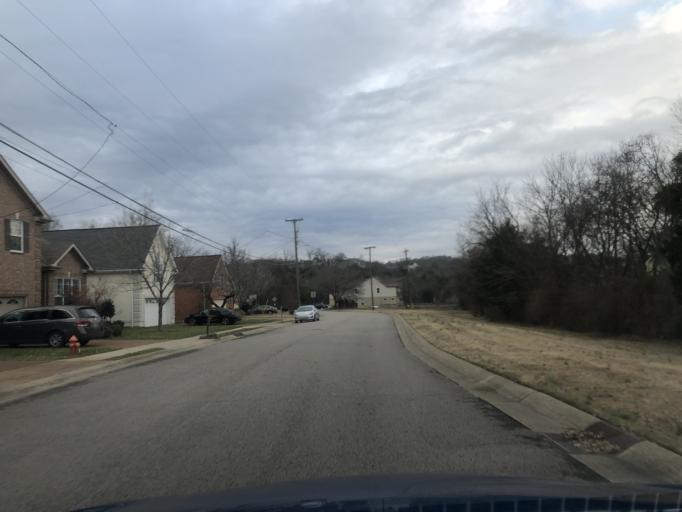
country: US
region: Tennessee
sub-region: Davidson County
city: Belle Meade
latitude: 36.1008
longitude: -86.9299
